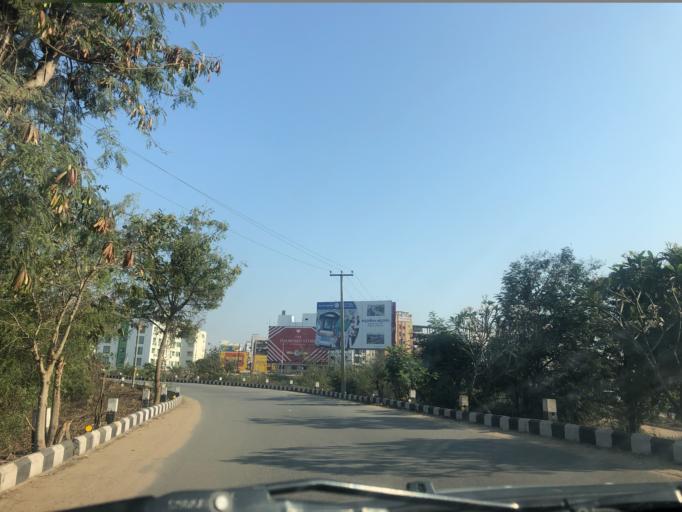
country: IN
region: Telangana
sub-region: Rangareddi
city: Sriramnagar
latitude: 17.2574
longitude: 78.3824
